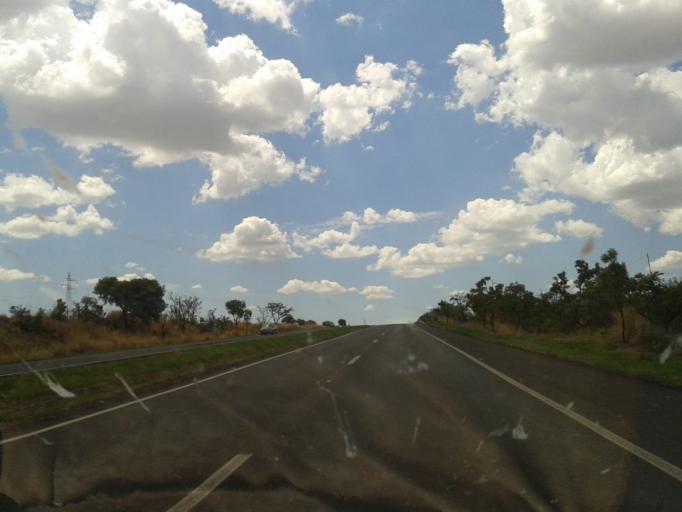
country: BR
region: Minas Gerais
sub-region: Uberlandia
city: Uberlandia
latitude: -19.1046
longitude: -48.1801
